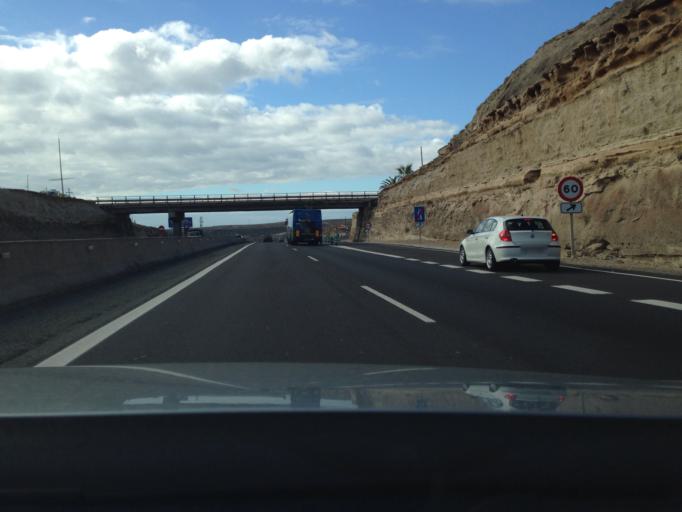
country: ES
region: Canary Islands
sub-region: Provincia de Santa Cruz de Tenerife
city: Lomo de Arico
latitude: 28.1688
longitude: -16.4335
